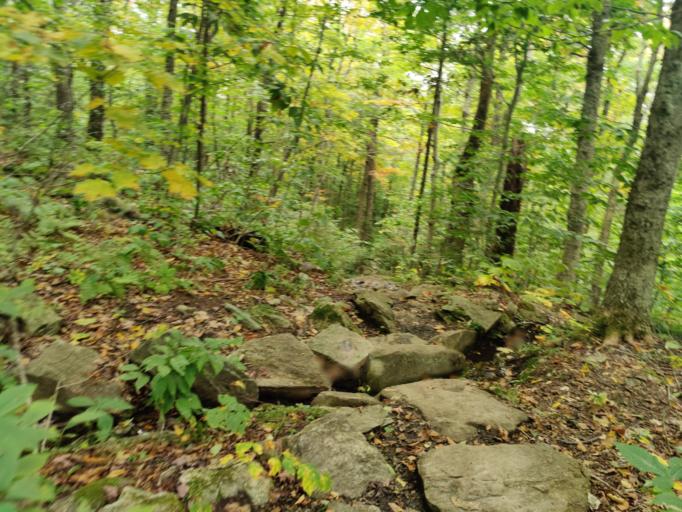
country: US
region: Vermont
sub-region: Bennington County
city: Manchester Center
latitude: 43.2622
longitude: -72.9403
